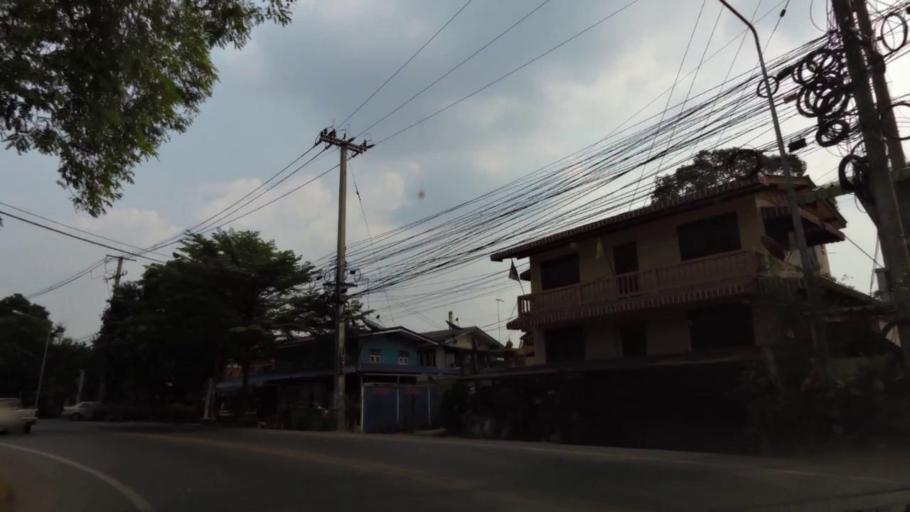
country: TH
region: Phra Nakhon Si Ayutthaya
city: Phra Nakhon Si Ayutthaya
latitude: 14.3333
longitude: 100.5779
